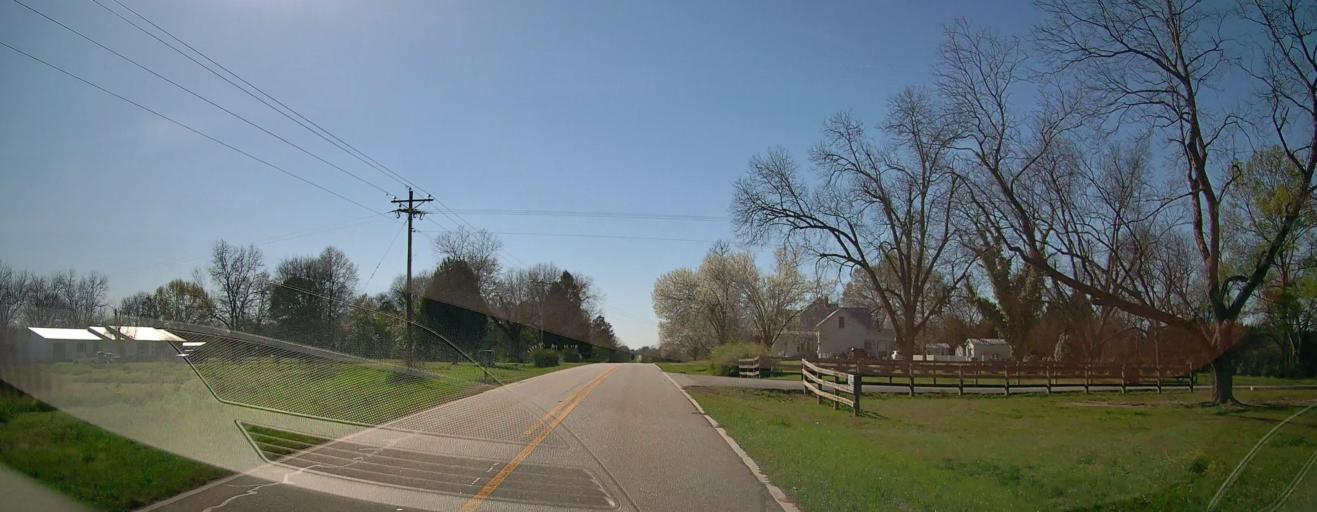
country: US
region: Georgia
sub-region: Peach County
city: Byron
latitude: 32.6443
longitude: -83.8299
